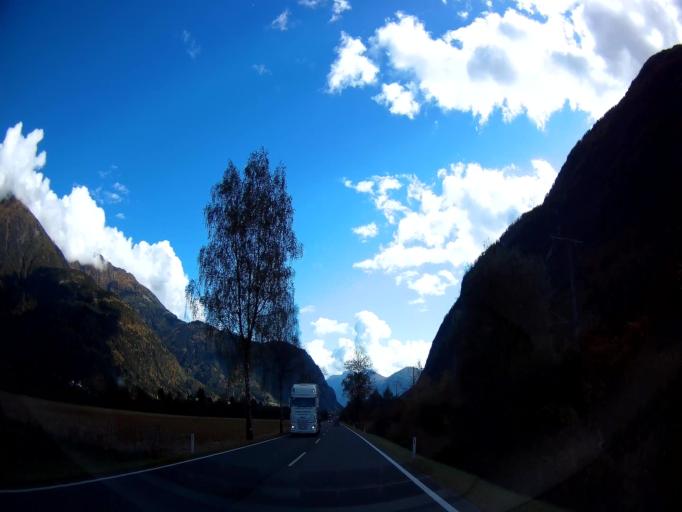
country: AT
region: Tyrol
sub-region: Politischer Bezirk Lienz
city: Nikolsdorf
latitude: 46.7836
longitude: 12.8853
